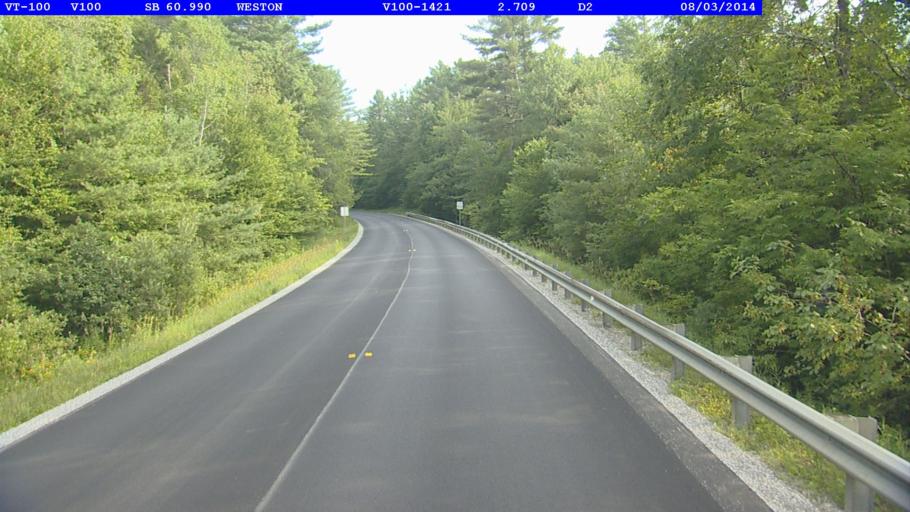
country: US
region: Vermont
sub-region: Windsor County
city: Chester
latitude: 43.2848
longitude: -72.7934
